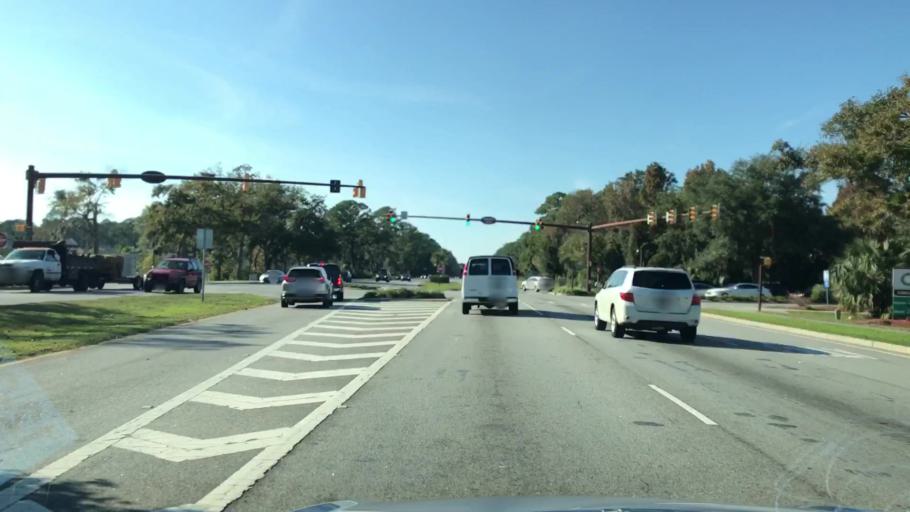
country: US
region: South Carolina
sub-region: Beaufort County
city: Hilton Head Island
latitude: 32.2152
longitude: -80.7020
